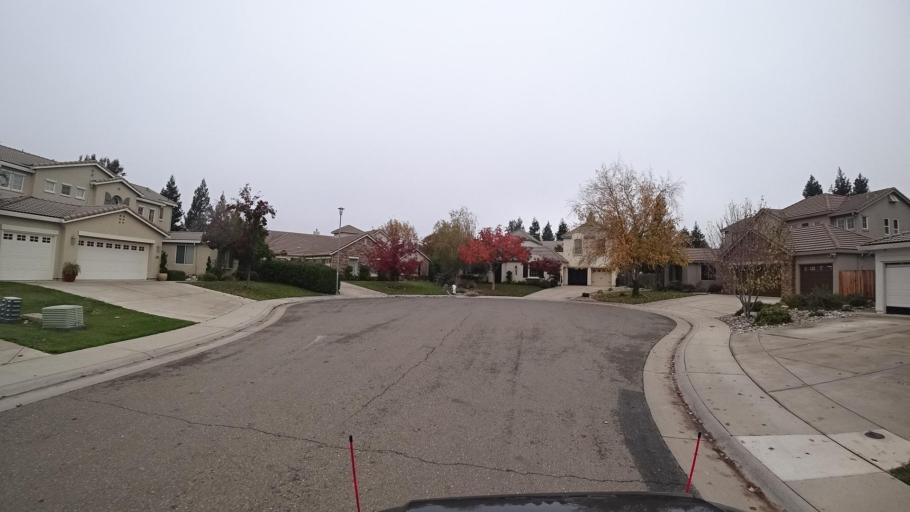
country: US
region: California
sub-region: Sacramento County
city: Elk Grove
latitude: 38.4082
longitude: -121.3383
